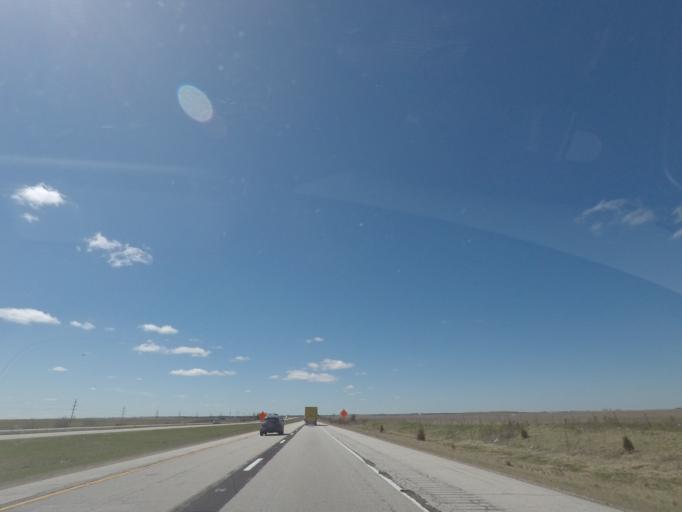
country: US
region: Illinois
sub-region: Livingston County
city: Odell
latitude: 40.9727
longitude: -88.5546
